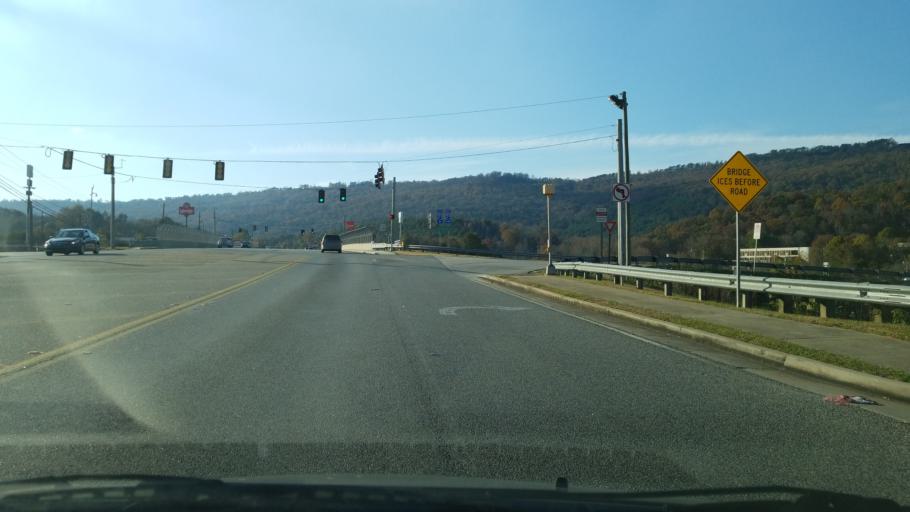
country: US
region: Georgia
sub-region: Dade County
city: Trenton
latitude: 34.8696
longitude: -85.5146
